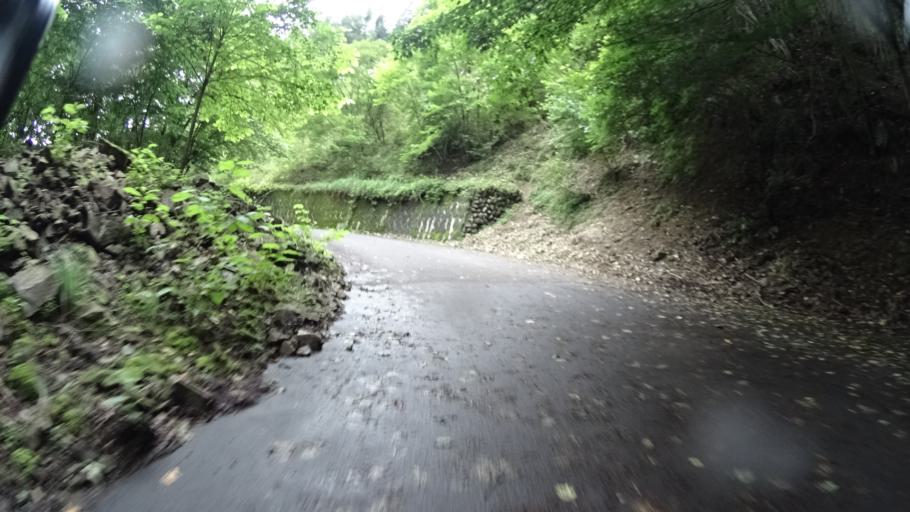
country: JP
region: Saitama
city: Chichibu
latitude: 35.8866
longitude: 139.1190
